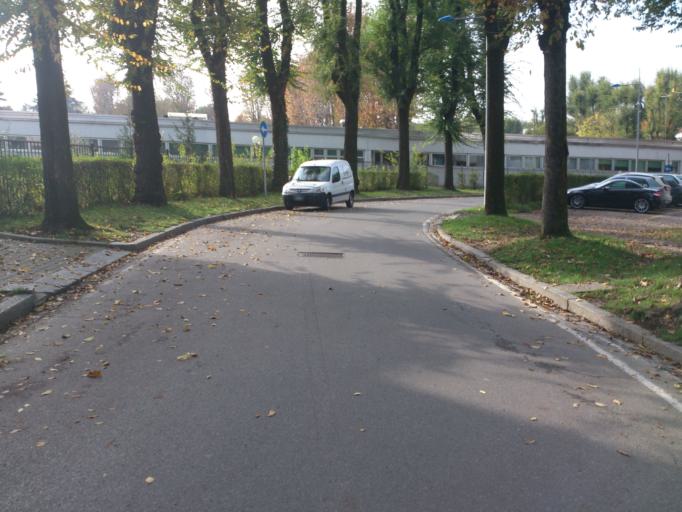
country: IT
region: Lombardy
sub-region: Citta metropolitana di Milano
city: San Donato Milanese
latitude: 45.4227
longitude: 9.2676
